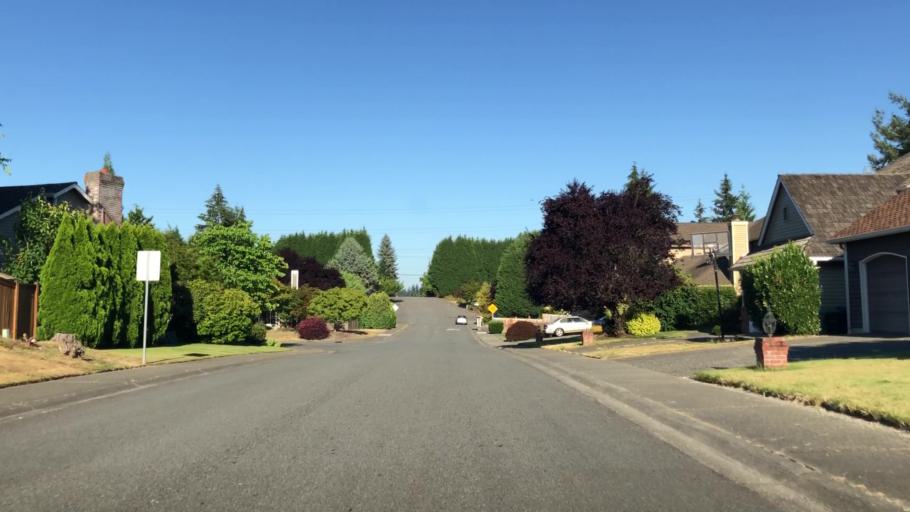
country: US
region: Washington
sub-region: King County
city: Woodinville
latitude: 47.7454
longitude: -122.1721
